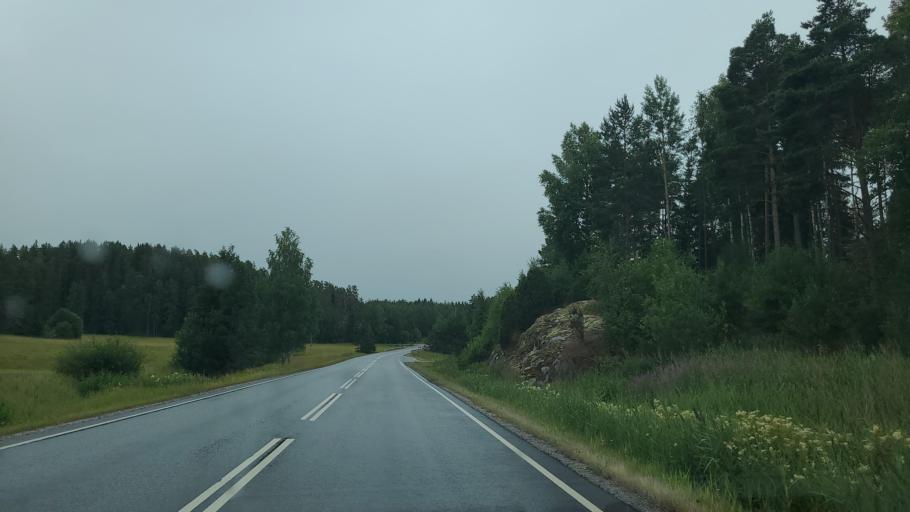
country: FI
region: Varsinais-Suomi
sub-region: Turku
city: Sauvo
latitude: 60.2756
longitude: 22.6689
